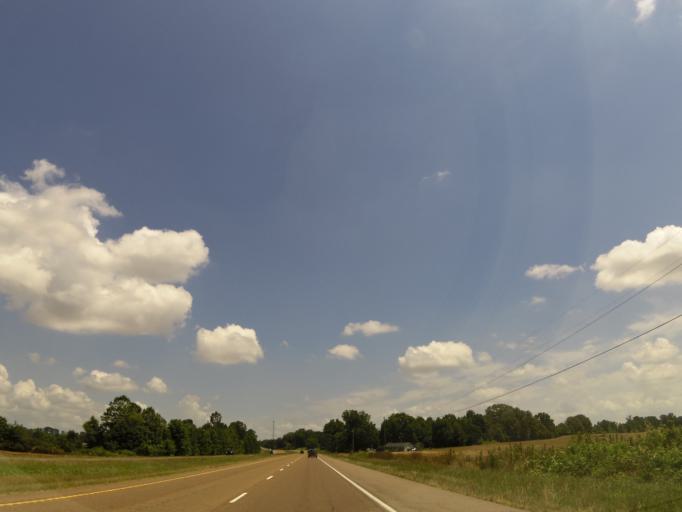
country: US
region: Tennessee
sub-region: Lauderdale County
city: Halls
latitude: 35.9209
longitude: -89.2766
